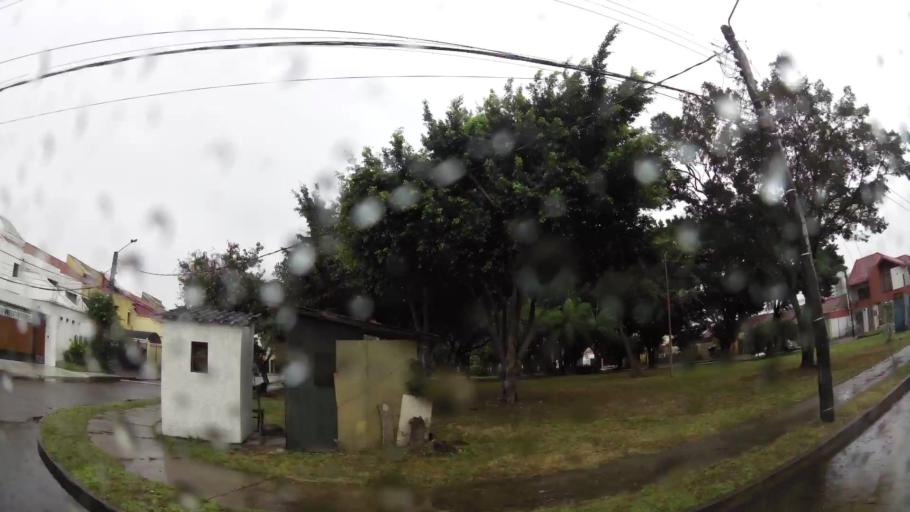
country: BO
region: Santa Cruz
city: Santa Cruz de la Sierra
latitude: -17.8077
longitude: -63.1605
